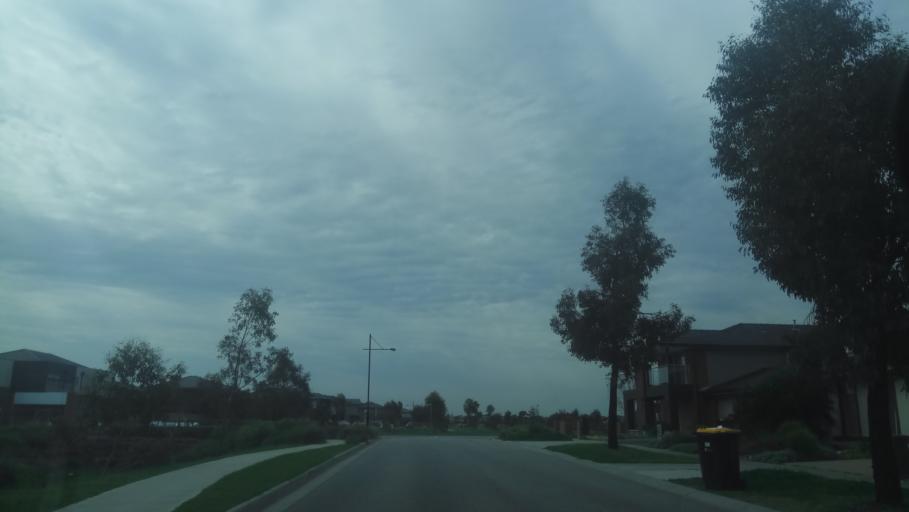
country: AU
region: Victoria
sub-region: Greater Dandenong
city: Keysborough
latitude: -38.0088
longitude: 145.1673
